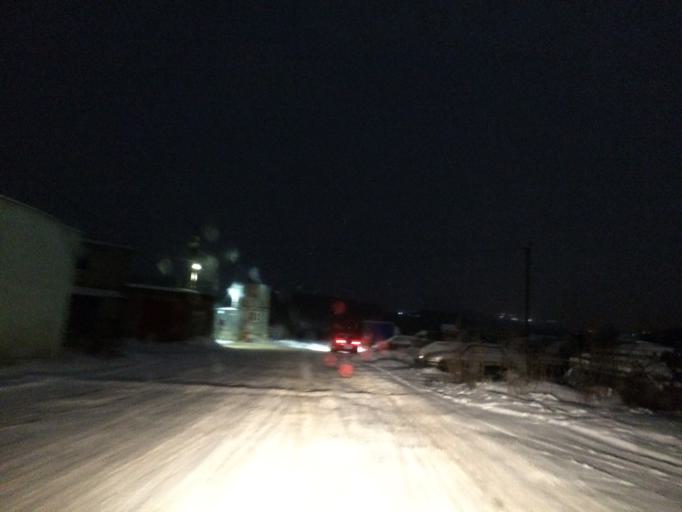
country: RU
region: Tula
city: Mendeleyevskiy
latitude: 54.1559
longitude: 37.6115
